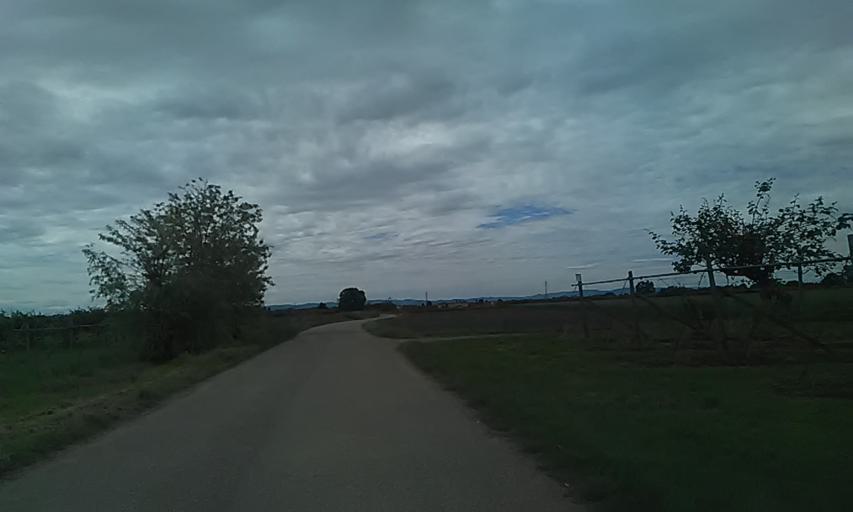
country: IT
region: Piedmont
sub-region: Provincia di Vercelli
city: Borgo d'Ale
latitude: 45.3352
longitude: 8.0510
